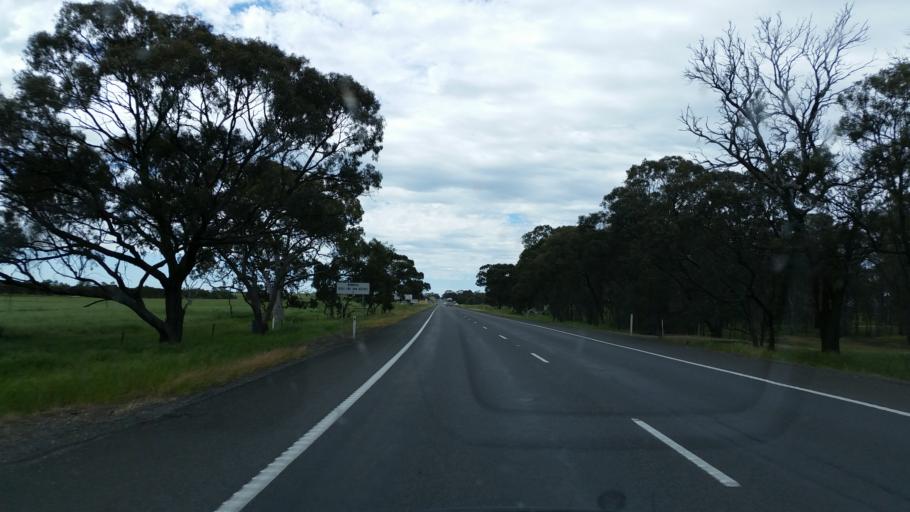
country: AU
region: South Australia
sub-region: Tatiara
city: Bordertown
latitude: -36.3455
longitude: 140.9730
